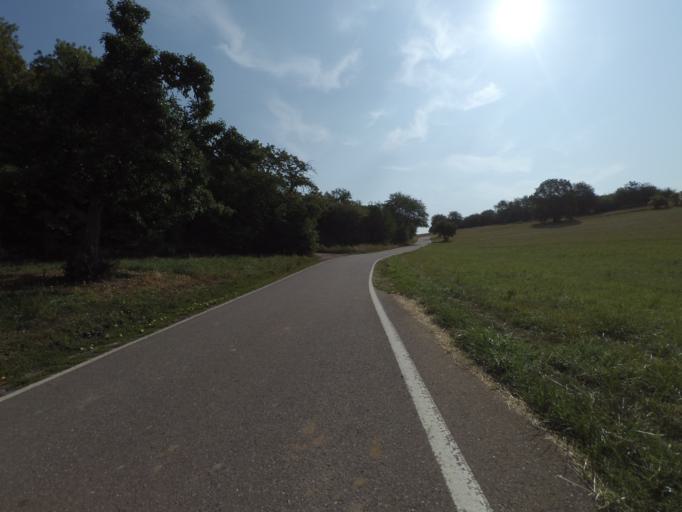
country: DE
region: Saarland
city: Perl
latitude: 49.5127
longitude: 6.4214
